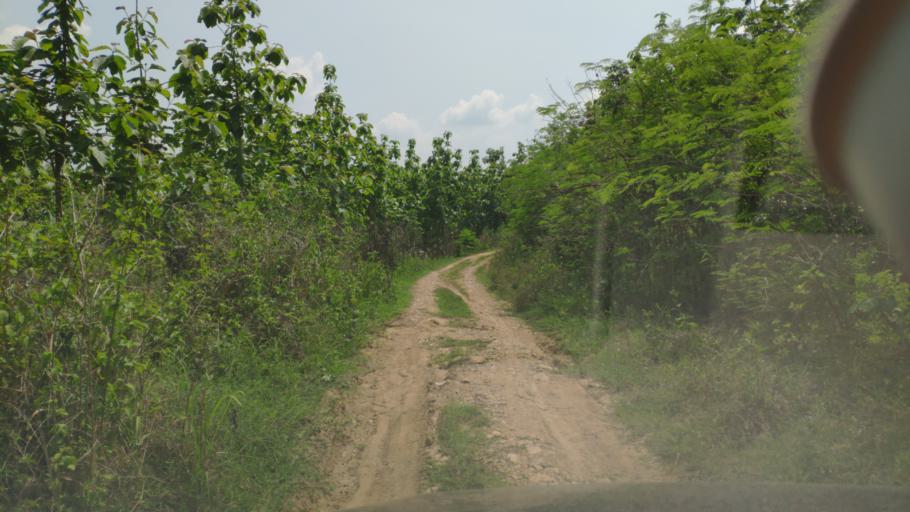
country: ID
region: Central Java
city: Gaplokan
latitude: -6.9110
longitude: 111.2685
